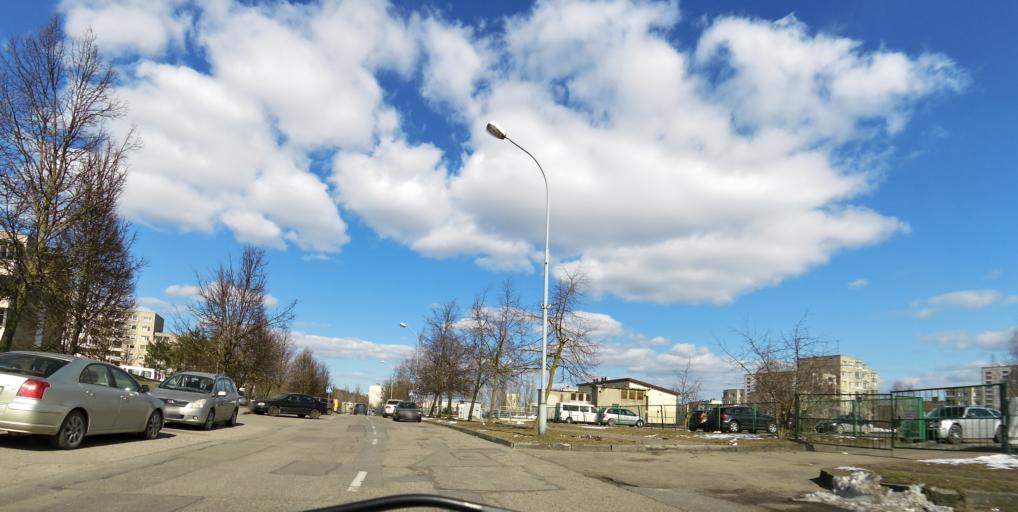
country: LT
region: Vilnius County
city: Pasilaiciai
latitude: 54.7264
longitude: 25.2255
